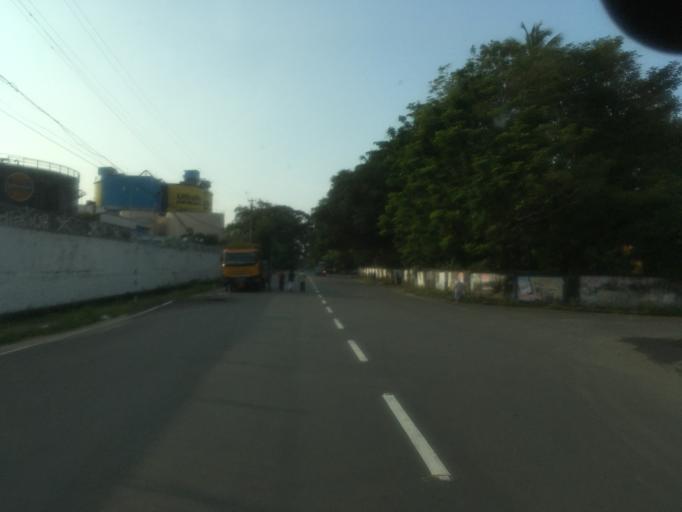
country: IN
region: Kerala
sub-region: Ernakulam
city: Cochin
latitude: 9.9669
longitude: 76.2627
